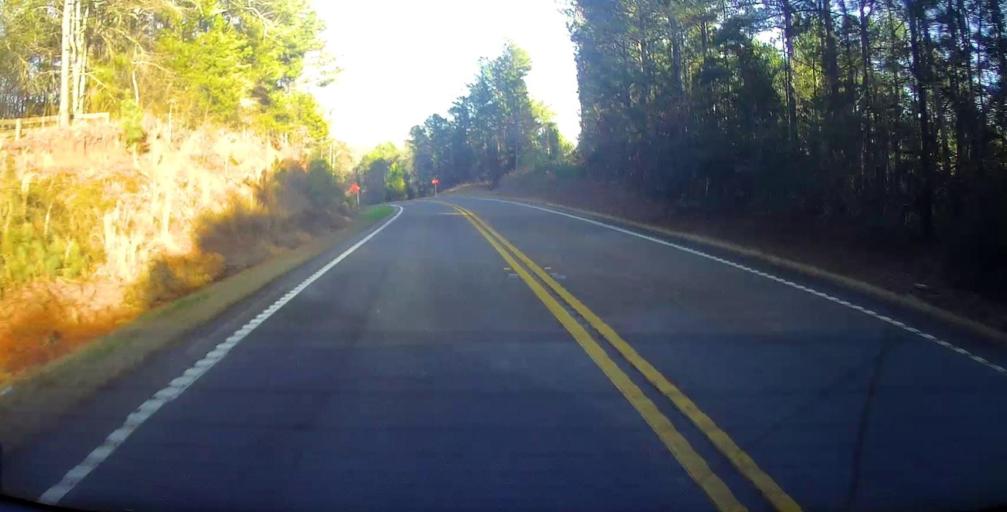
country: US
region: Georgia
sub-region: Upson County
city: Thomaston
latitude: 32.8622
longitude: -84.4115
